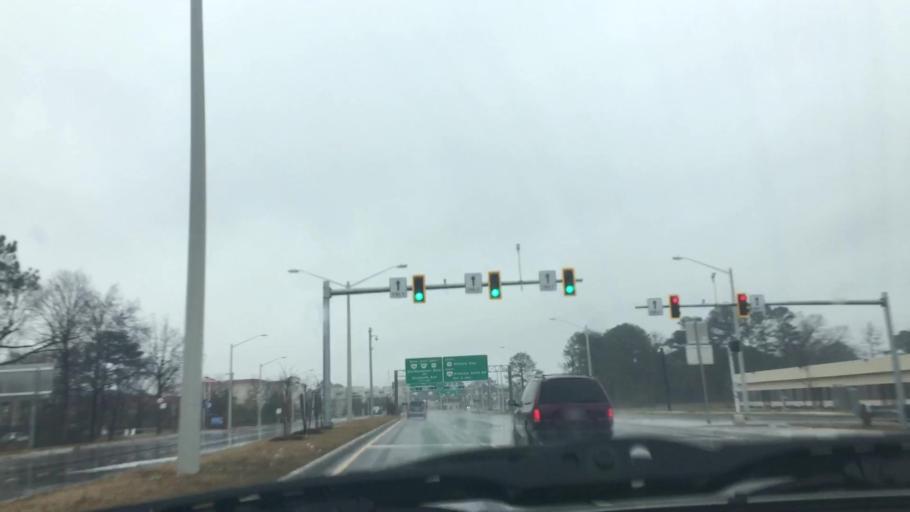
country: US
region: Virginia
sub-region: City of Norfolk
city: Norfolk
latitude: 36.8785
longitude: -76.2111
